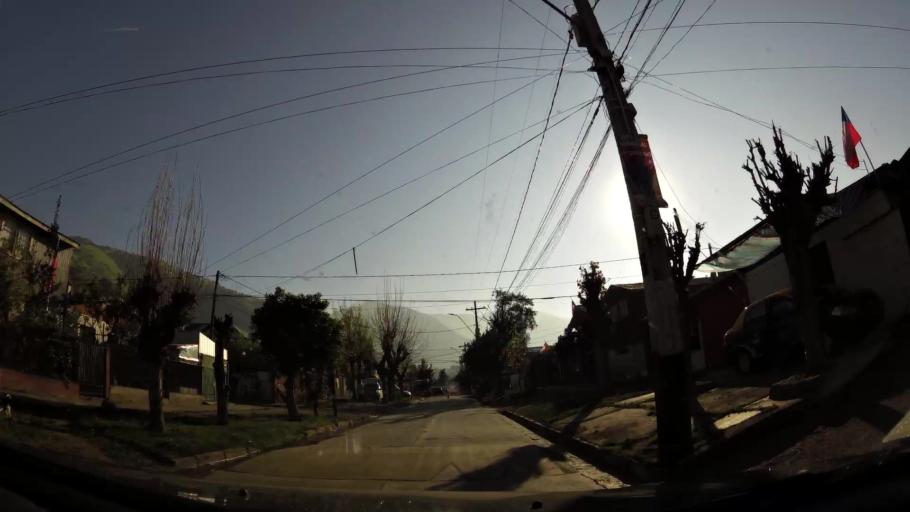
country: CL
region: Santiago Metropolitan
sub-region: Provincia de Chacabuco
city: Chicureo Abajo
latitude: -33.3646
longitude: -70.6382
